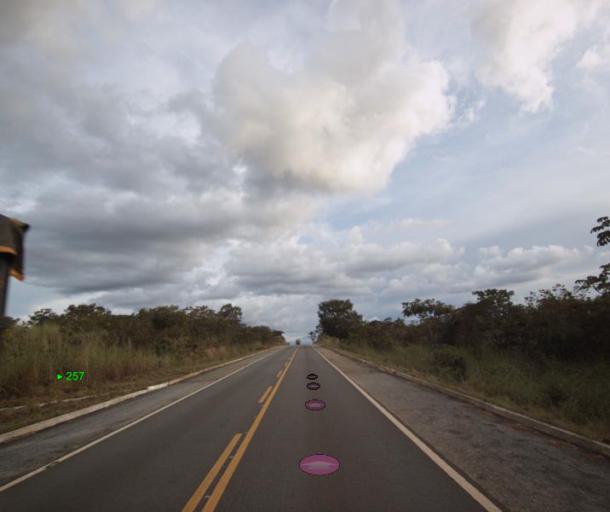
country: BR
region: Goias
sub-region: Barro Alto
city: Barro Alto
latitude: -14.8907
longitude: -48.6414
